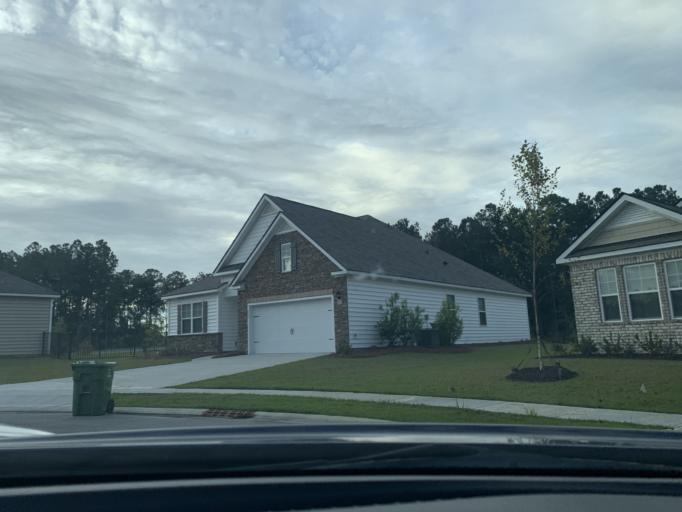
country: US
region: Georgia
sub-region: Chatham County
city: Pooler
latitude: 32.0698
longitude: -81.2563
